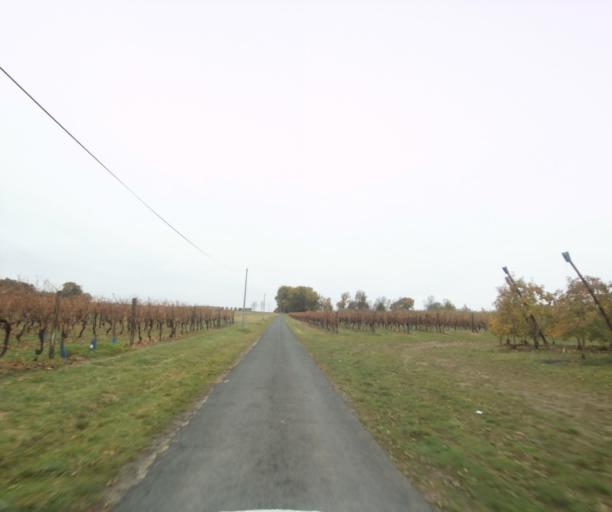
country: FR
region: Poitou-Charentes
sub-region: Departement de la Charente-Maritime
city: Chermignac
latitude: 45.7109
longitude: -0.6813
